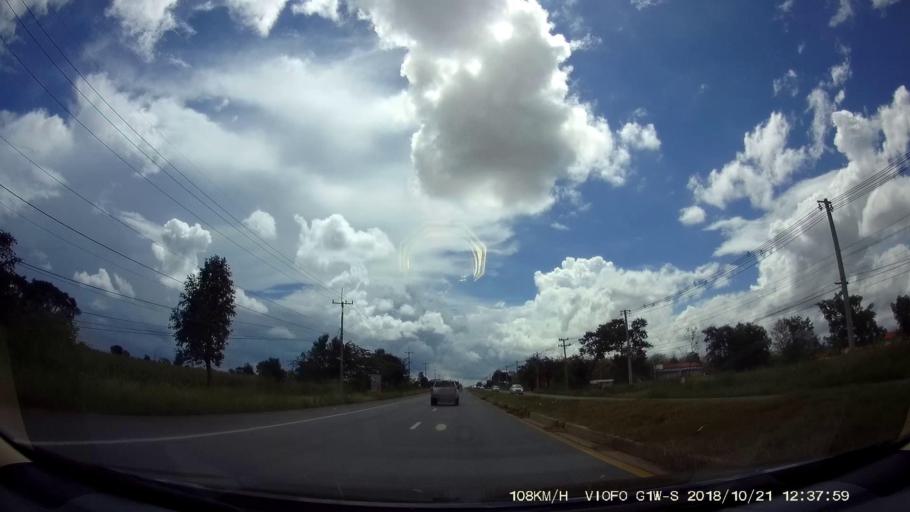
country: TH
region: Nakhon Ratchasima
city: Dan Khun Thot
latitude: 15.0606
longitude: 101.7084
